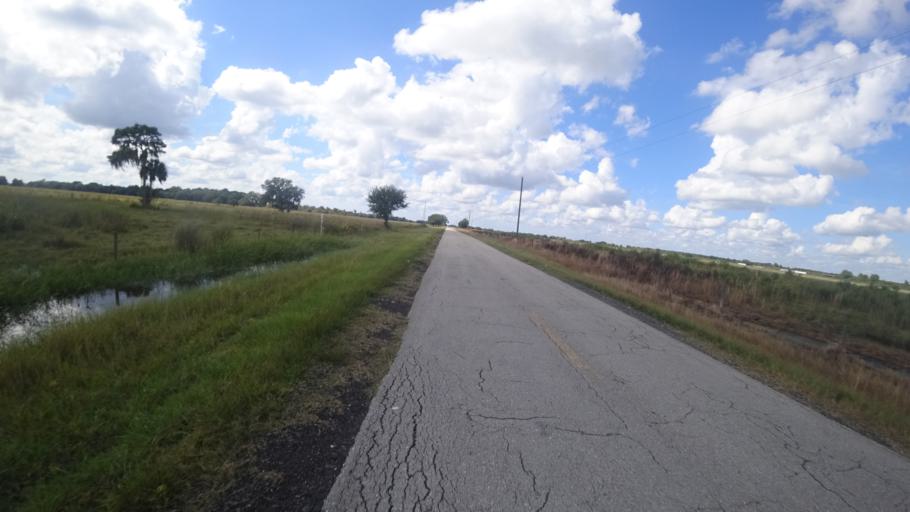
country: US
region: Florida
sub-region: Sarasota County
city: Warm Mineral Springs
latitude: 27.2737
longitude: -82.1664
